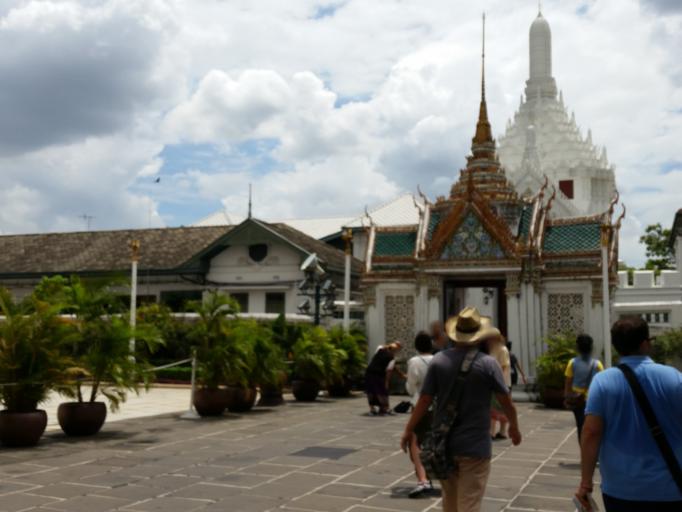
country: TH
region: Bangkok
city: Bangkok
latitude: 13.7504
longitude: 100.4905
